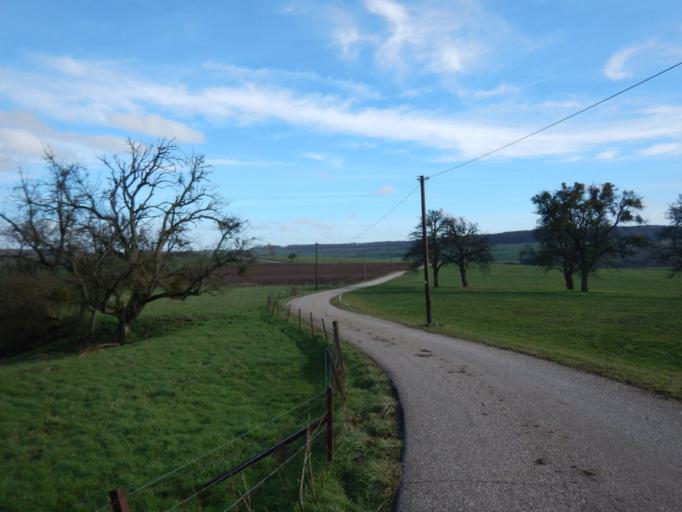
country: LU
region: Grevenmacher
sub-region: Canton d'Echternach
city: Echternach
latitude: 49.7845
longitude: 6.4178
